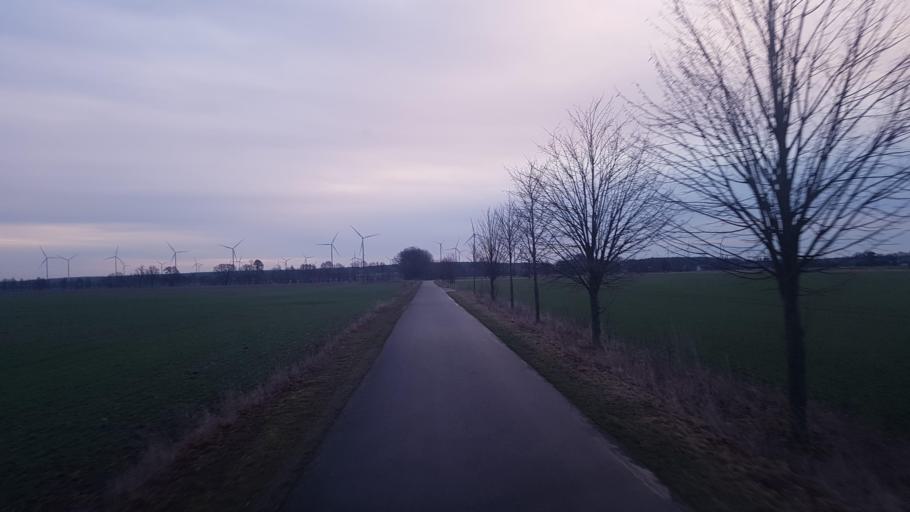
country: DE
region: Brandenburg
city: Dahme
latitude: 51.8697
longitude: 13.4444
